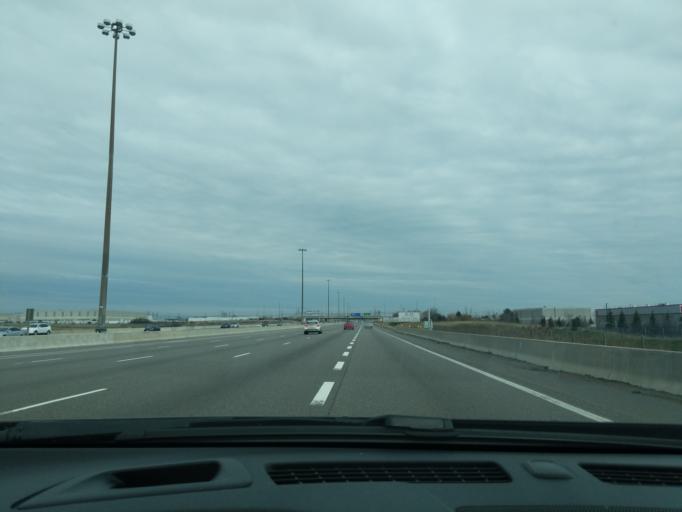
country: CA
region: Ontario
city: Mississauga
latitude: 43.6554
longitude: -79.6818
